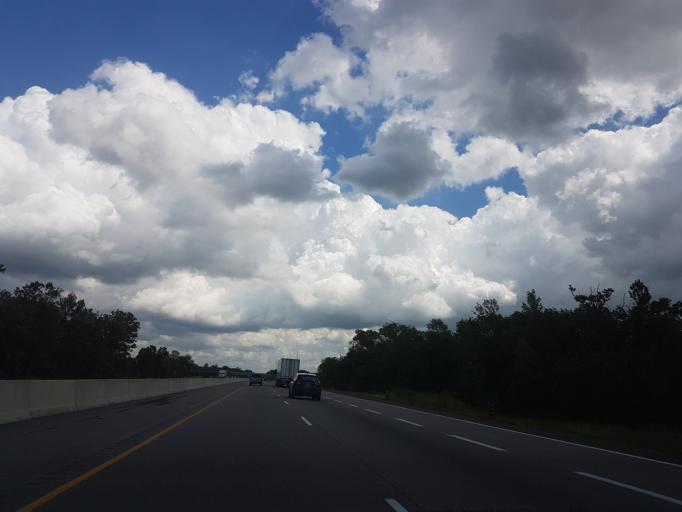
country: CA
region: Ontario
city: Belleville
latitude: 44.2187
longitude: -77.2499
